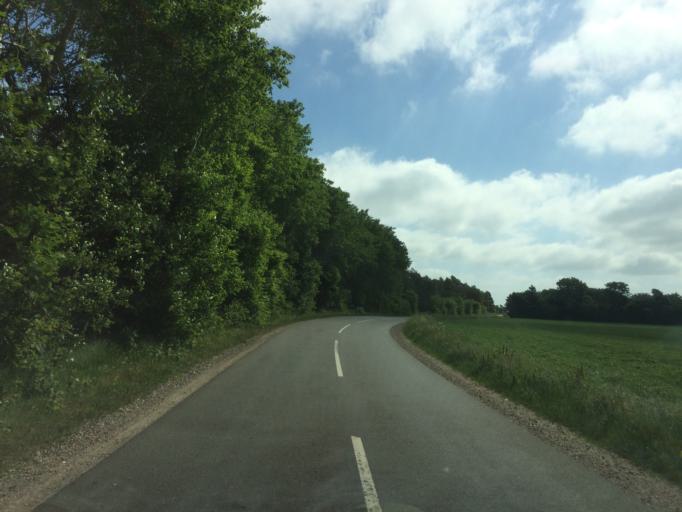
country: DK
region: Central Jutland
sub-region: Holstebro Kommune
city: Ulfborg
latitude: 56.2052
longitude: 8.4658
